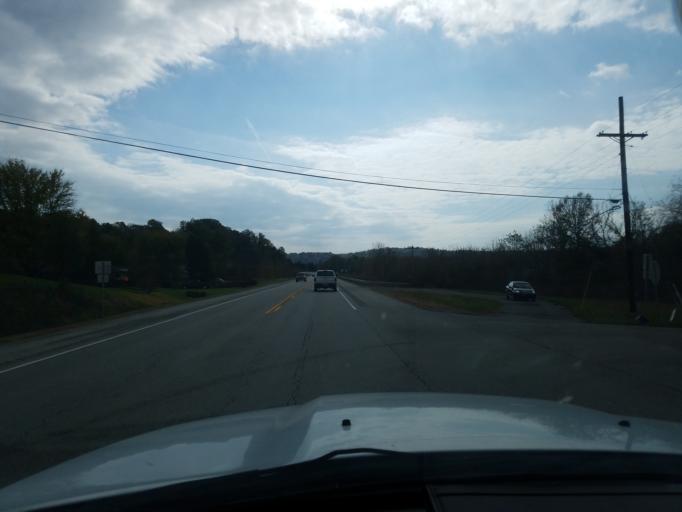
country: US
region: Kentucky
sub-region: Bullitt County
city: Mount Washington
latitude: 38.0193
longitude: -85.5221
